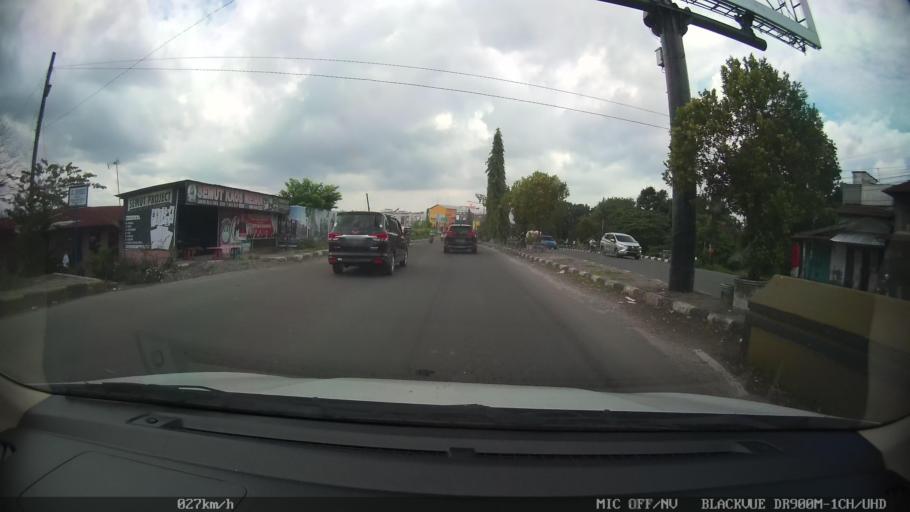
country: ID
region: North Sumatra
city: Medan
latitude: 3.6270
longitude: 98.6646
